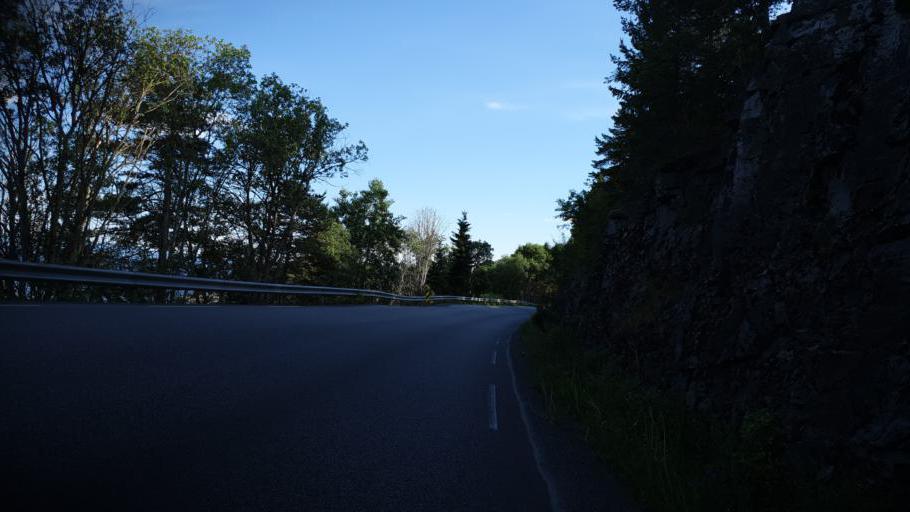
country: NO
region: Sor-Trondelag
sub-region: Trondheim
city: Trondheim
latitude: 63.5758
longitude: 10.4185
